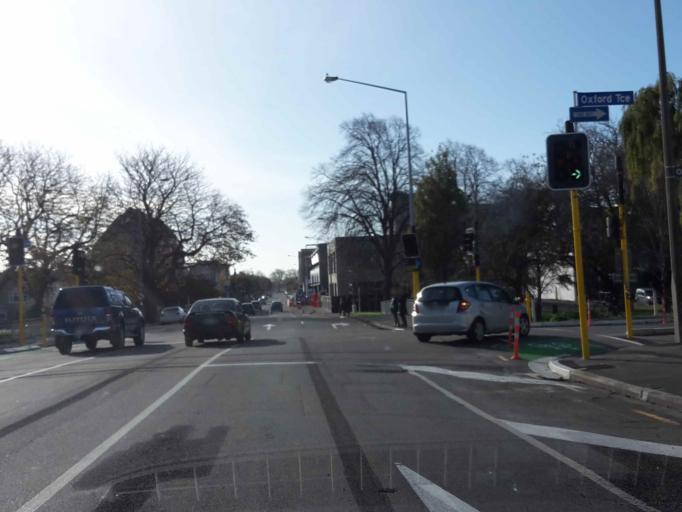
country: NZ
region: Canterbury
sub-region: Christchurch City
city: Christchurch
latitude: -43.5353
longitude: 172.6307
